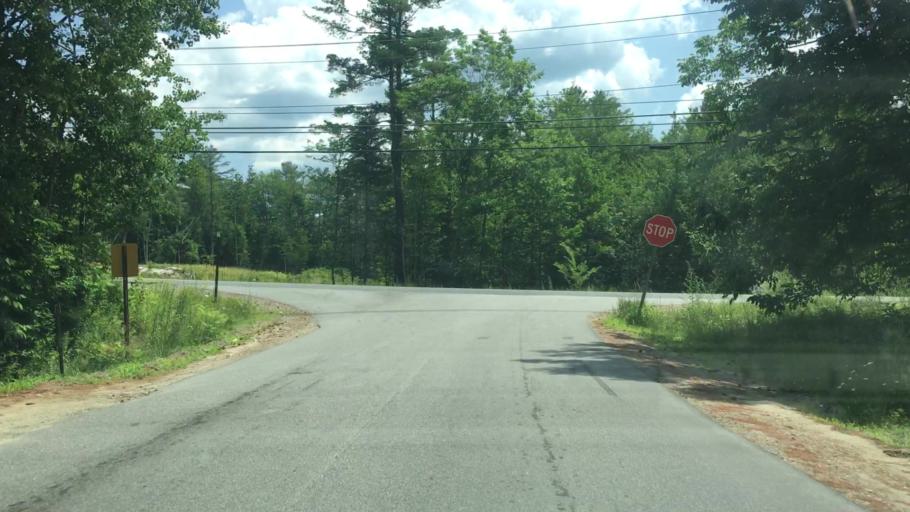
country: US
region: New Hampshire
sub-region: Grafton County
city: Enfield
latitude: 43.6527
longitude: -72.0928
